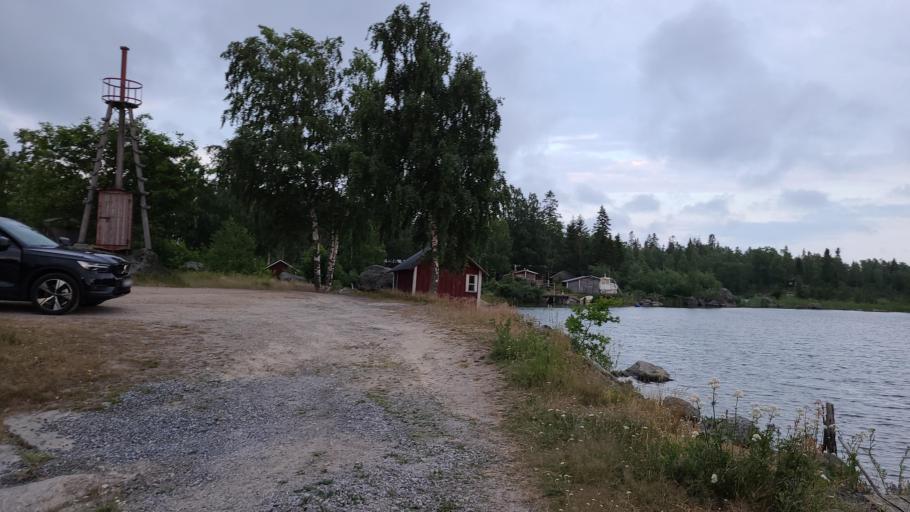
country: FI
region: Ostrobothnia
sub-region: Vaasa
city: Replot
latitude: 63.3237
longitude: 21.1387
